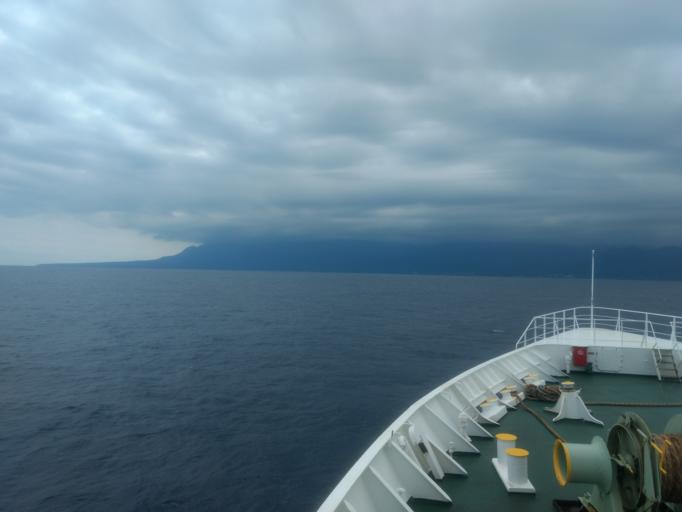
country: JP
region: Kagoshima
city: Nishinoomote
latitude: 30.4980
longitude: 130.6079
